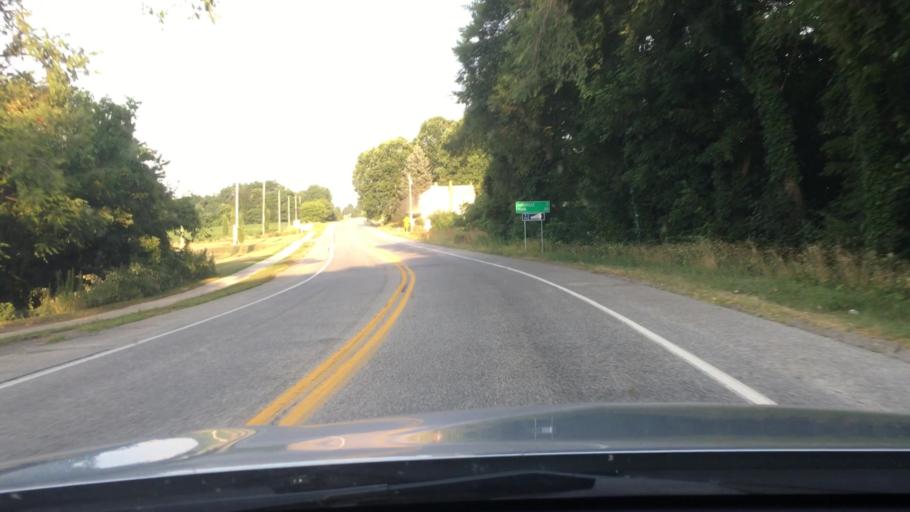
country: US
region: Pennsylvania
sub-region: York County
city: Dillsburg
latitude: 40.1075
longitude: -77.0308
